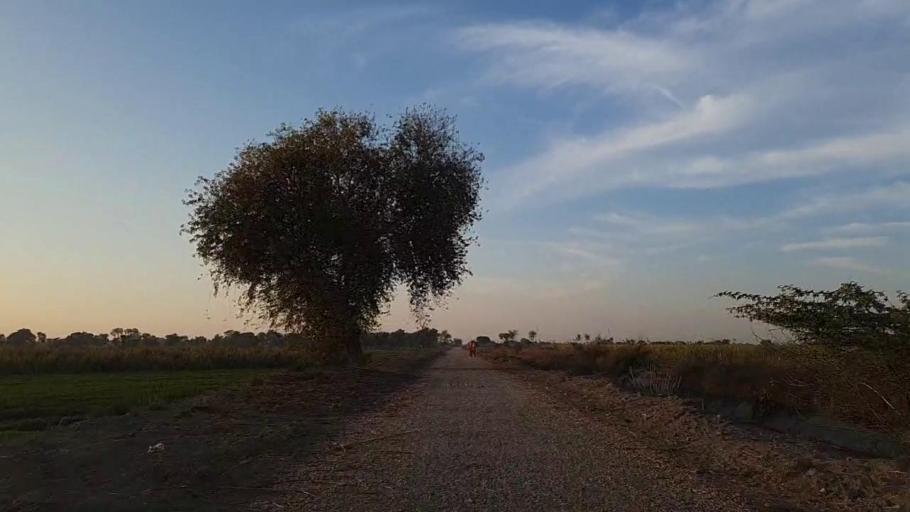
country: PK
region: Sindh
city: Bandhi
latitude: 26.6182
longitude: 68.3519
